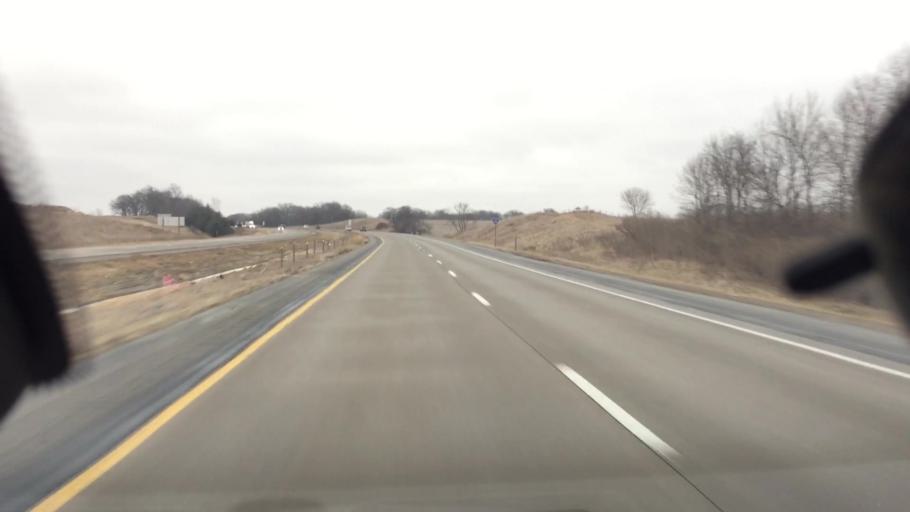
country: US
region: Iowa
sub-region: Cedar County
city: West Branch
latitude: 41.6749
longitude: -91.4372
